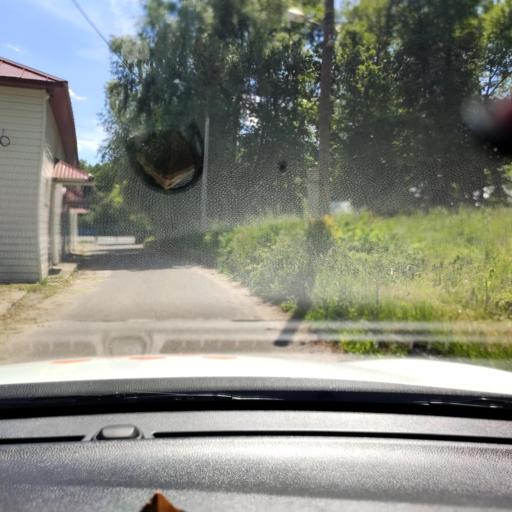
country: RU
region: Tatarstan
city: Sviyazhsk
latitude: 55.7782
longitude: 48.7899
